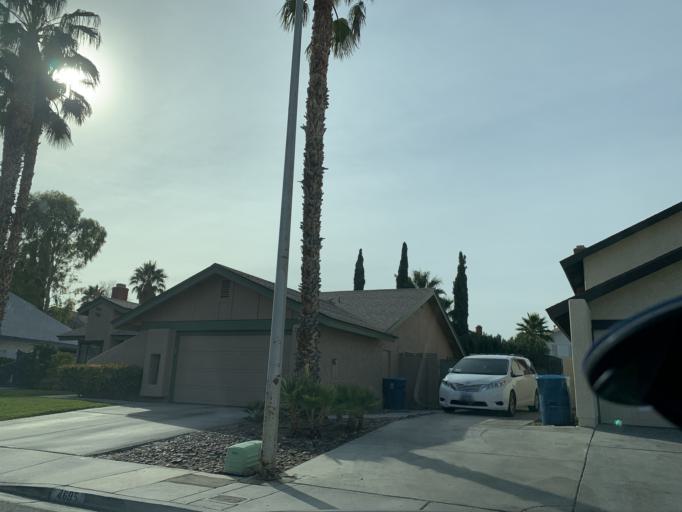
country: US
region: Nevada
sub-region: Clark County
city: Spring Valley
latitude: 36.1038
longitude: -115.2366
